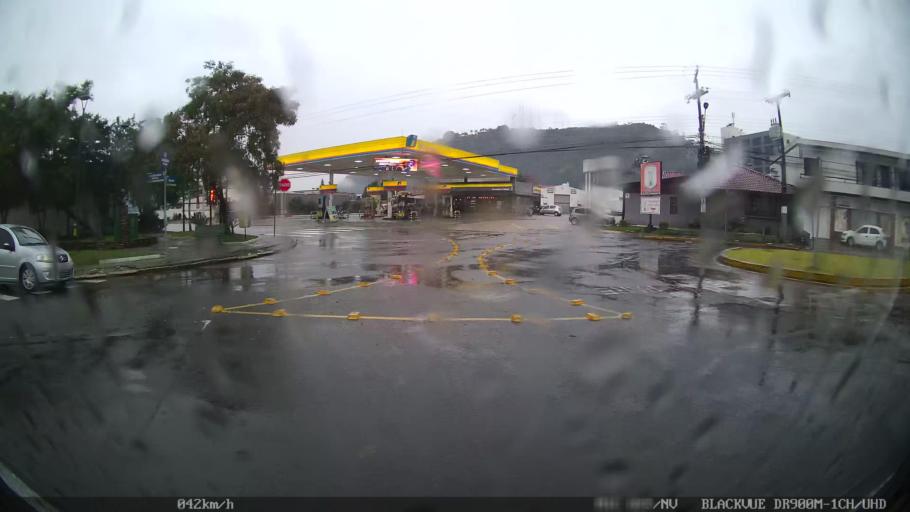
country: BR
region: Santa Catarina
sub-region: Itajai
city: Itajai
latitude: -26.9180
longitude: -48.6708
